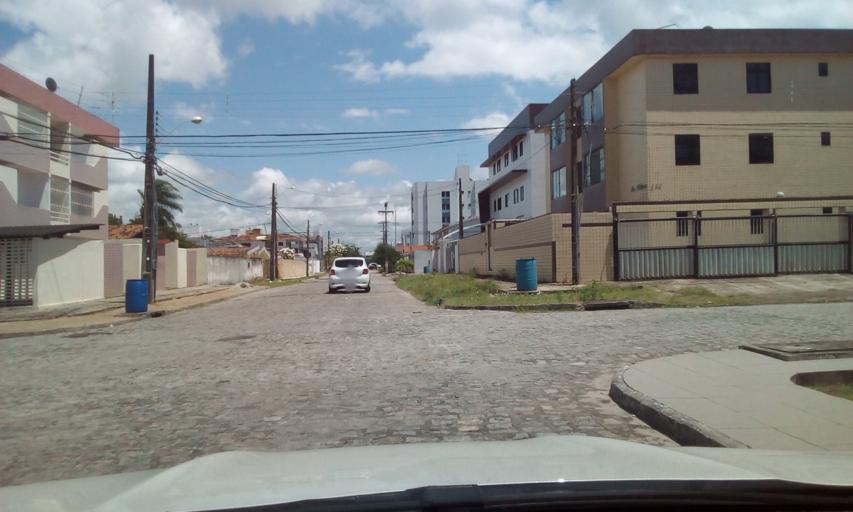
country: BR
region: Paraiba
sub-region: Joao Pessoa
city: Joao Pessoa
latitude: -7.0713
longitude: -34.8430
